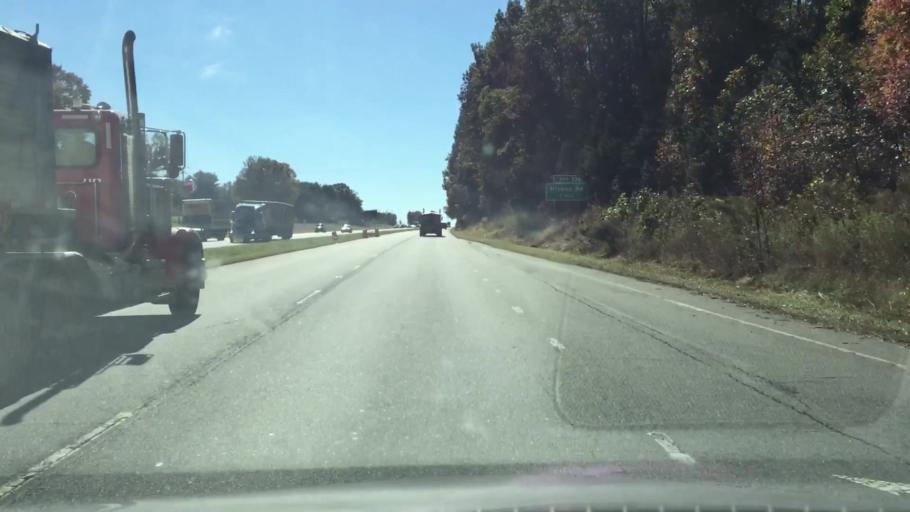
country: US
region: North Carolina
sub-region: Guilford County
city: McLeansville
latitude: 36.1711
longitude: -79.7149
